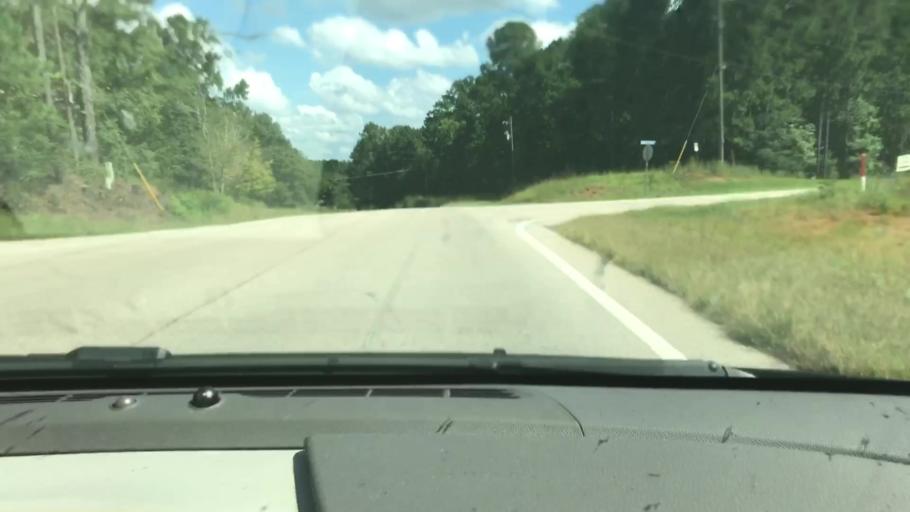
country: US
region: Georgia
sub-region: Troup County
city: La Grange
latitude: 32.9161
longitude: -85.0201
